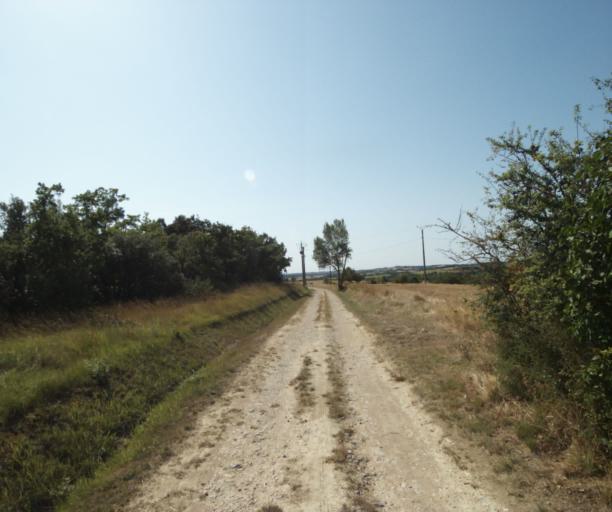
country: FR
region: Midi-Pyrenees
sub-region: Departement de la Haute-Garonne
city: Saint-Felix-Lauragais
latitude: 43.4401
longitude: 1.8341
